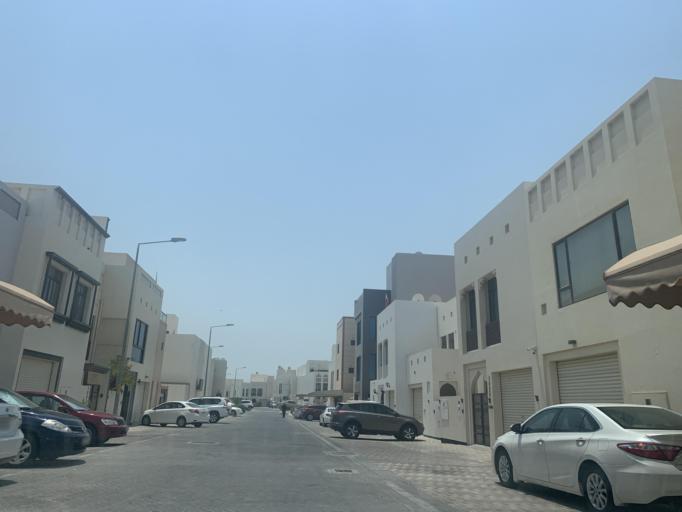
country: BH
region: Muharraq
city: Al Hadd
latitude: 26.2383
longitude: 50.6737
